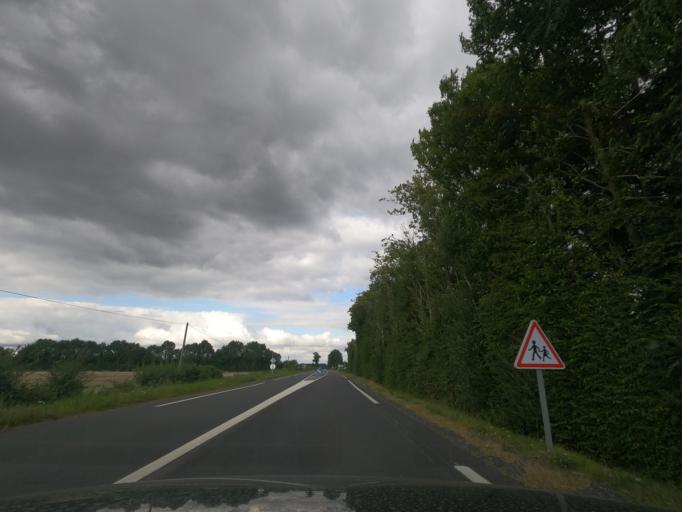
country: FR
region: Lower Normandy
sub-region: Departement de l'Orne
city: Gace
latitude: 48.8556
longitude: 0.3617
